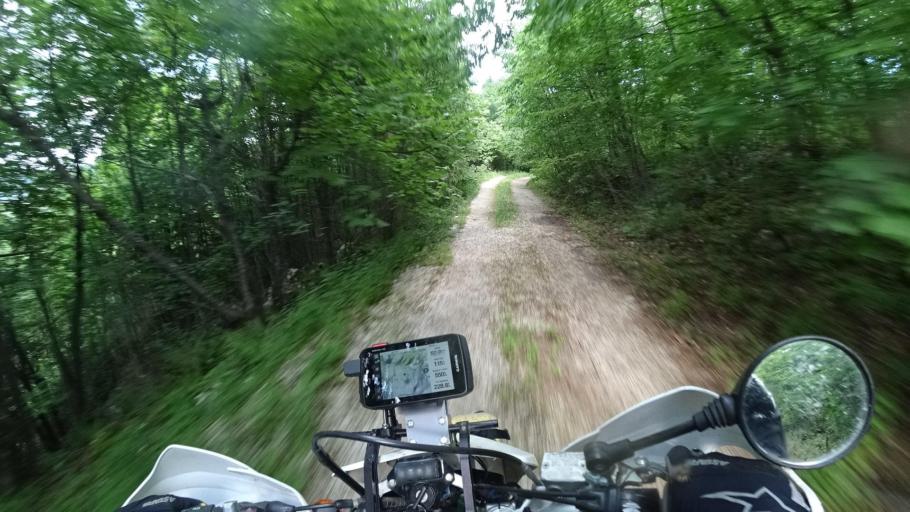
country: BA
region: Federation of Bosnia and Herzegovina
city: Bosanska Krupa
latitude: 44.7532
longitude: 16.3834
